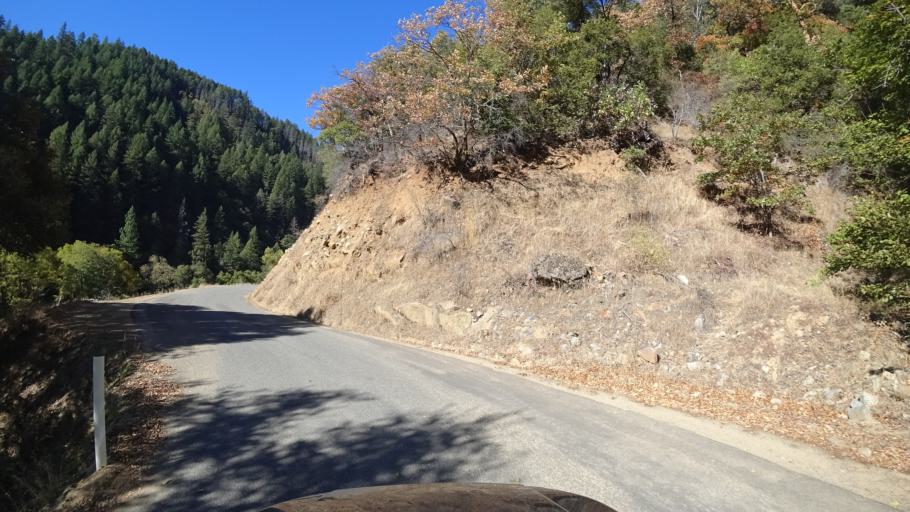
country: US
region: California
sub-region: Humboldt County
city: Willow Creek
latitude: 41.2319
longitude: -123.2567
